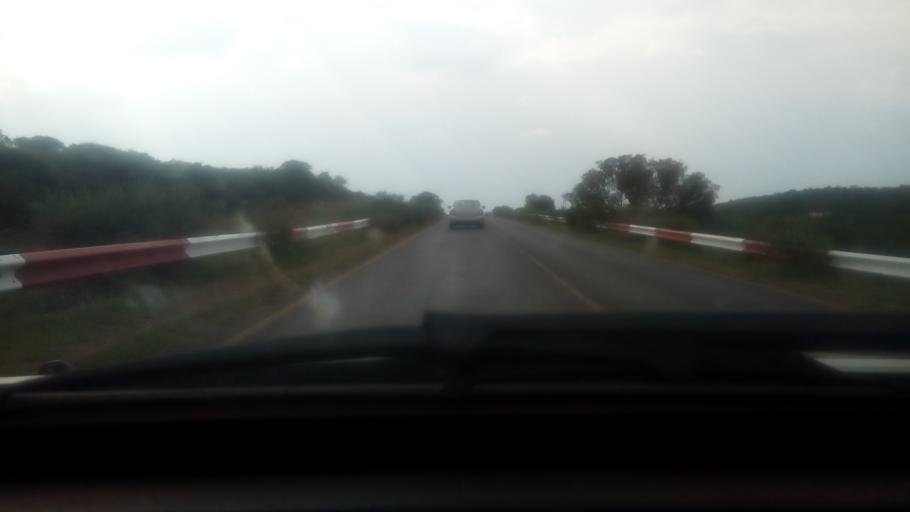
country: BW
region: Kweneng
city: Molepolole
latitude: -24.4108
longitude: 25.5982
